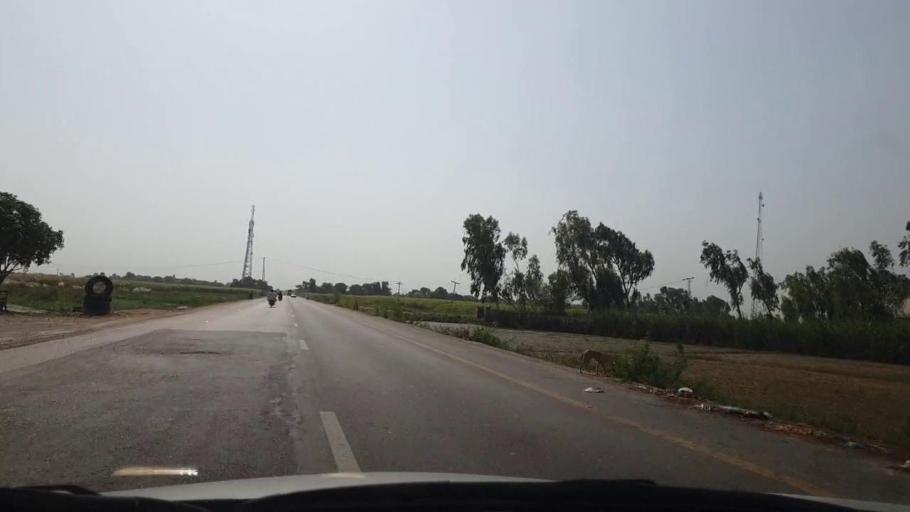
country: PK
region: Sindh
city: Tando Muhammad Khan
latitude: 25.0928
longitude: 68.5979
